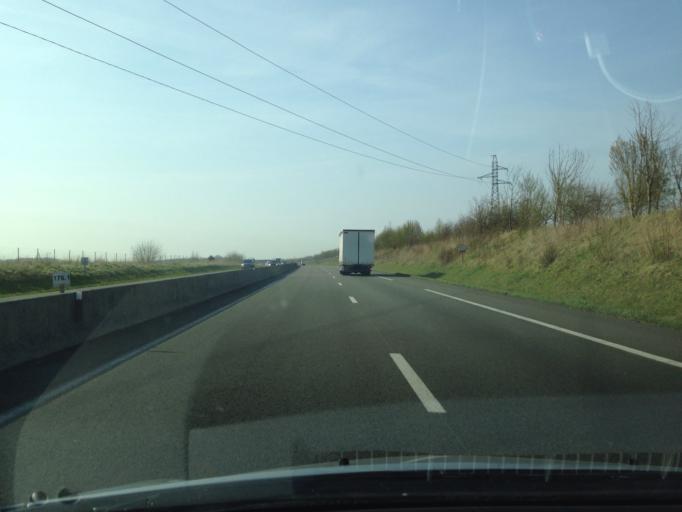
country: FR
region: Picardie
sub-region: Departement de la Somme
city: Sailly-Flibeaucourt
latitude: 50.1529
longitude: 1.7933
